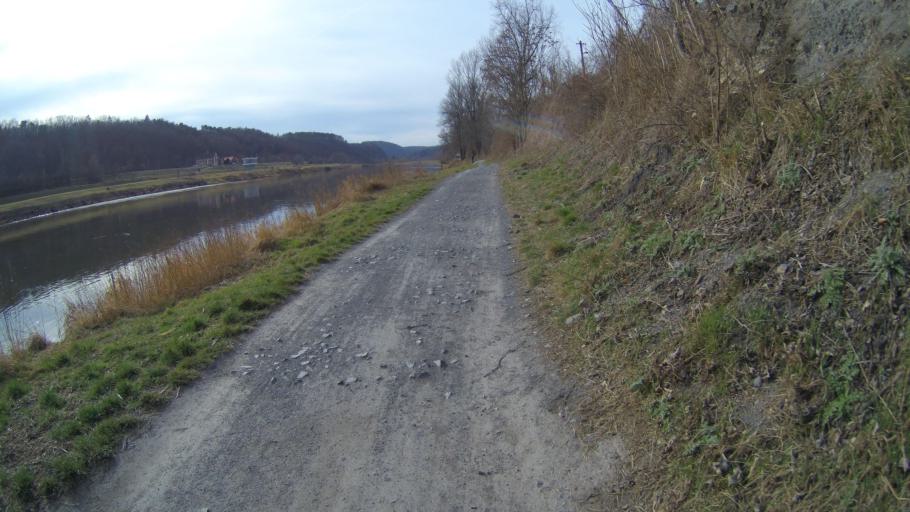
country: CZ
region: Central Bohemia
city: Roztoky
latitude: 50.1732
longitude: 14.3943
